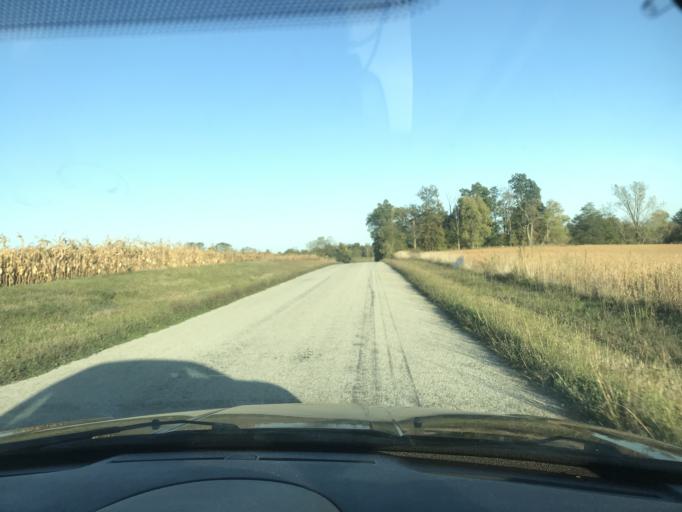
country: US
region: Ohio
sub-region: Logan County
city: West Liberty
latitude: 40.2332
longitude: -83.8288
